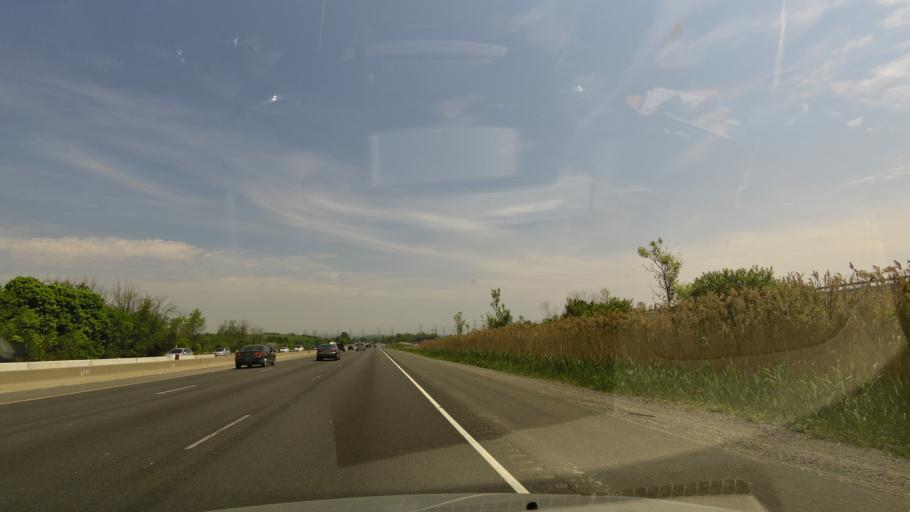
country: CA
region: Ontario
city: Oshawa
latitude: 43.8839
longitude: -78.7216
